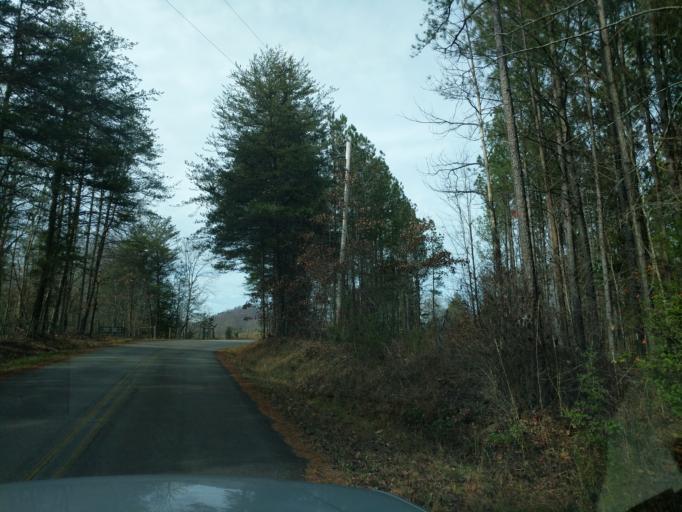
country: US
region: South Carolina
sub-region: Oconee County
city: Walhalla
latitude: 34.8587
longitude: -83.0556
